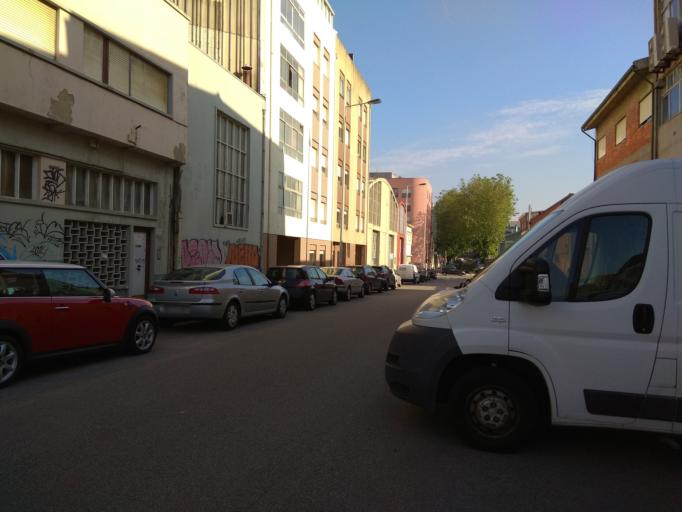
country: PT
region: Porto
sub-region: Matosinhos
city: Matosinhos
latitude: 41.1760
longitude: -8.6851
